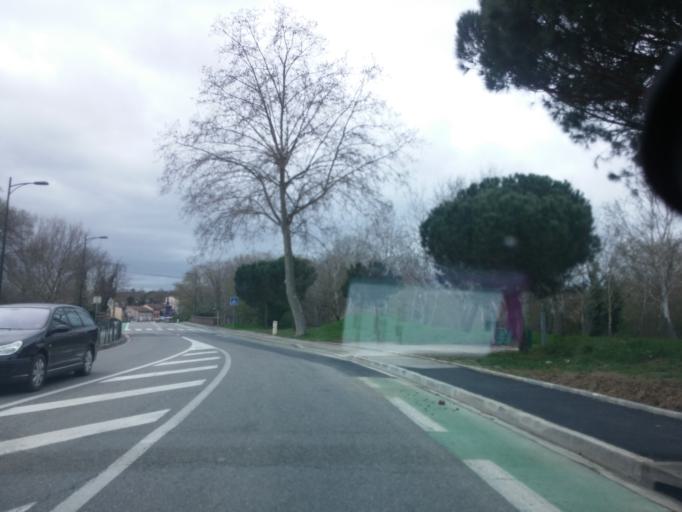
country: FR
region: Midi-Pyrenees
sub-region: Departement de la Haute-Garonne
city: Blagnac
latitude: 43.6088
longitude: 1.3860
